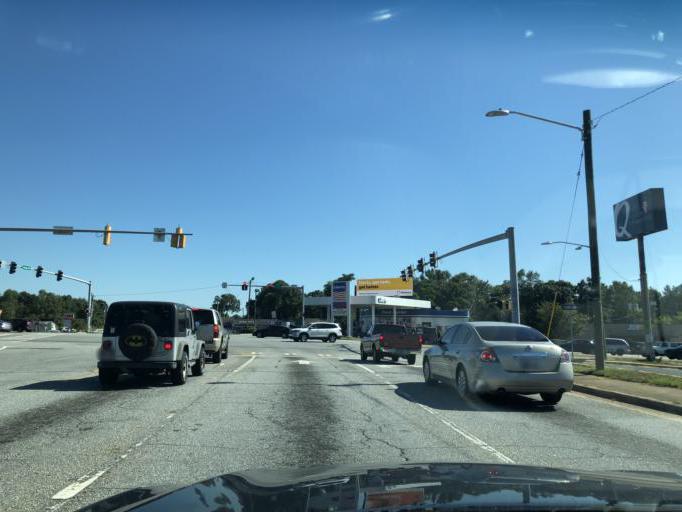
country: US
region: Georgia
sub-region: Muscogee County
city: Columbus
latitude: 32.5073
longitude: -84.9535
